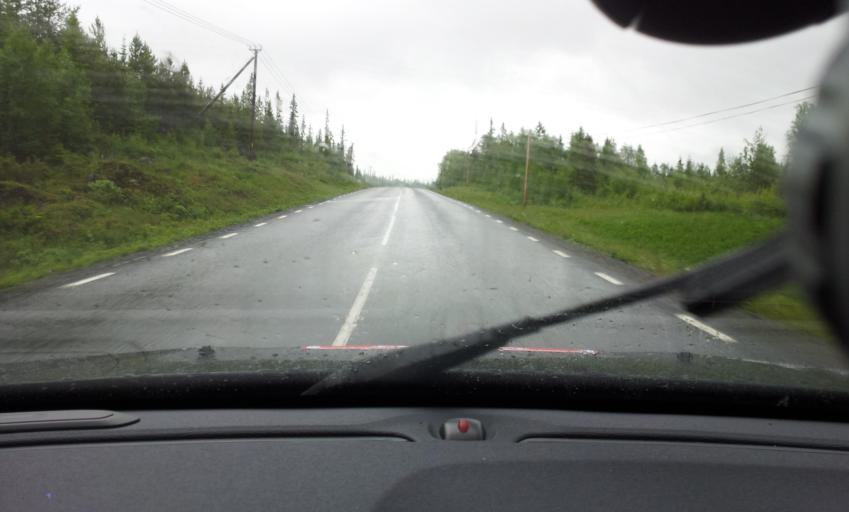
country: SE
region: Jaemtland
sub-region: Are Kommun
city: Are
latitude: 63.2385
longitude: 13.1752
